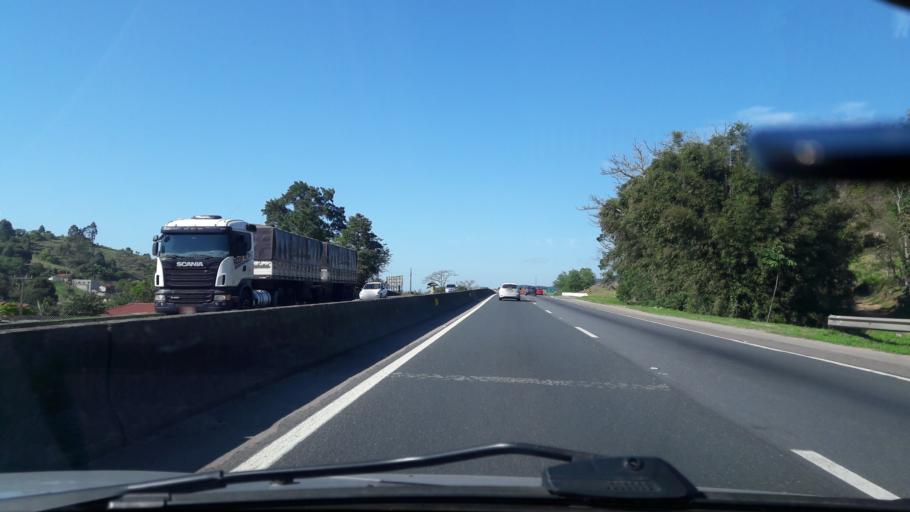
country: BR
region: Santa Catarina
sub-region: Tijucas
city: Tijucas
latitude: -27.2884
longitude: -48.6309
